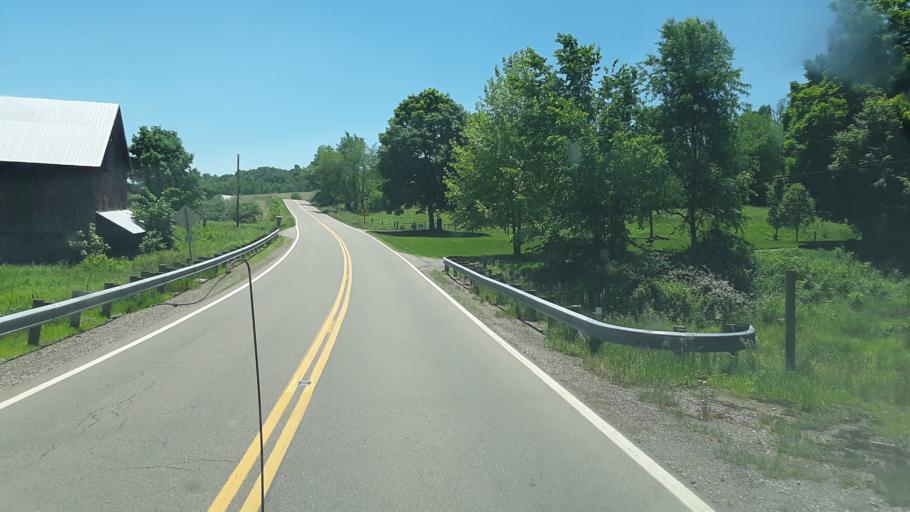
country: US
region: Ohio
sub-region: Coshocton County
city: Coshocton
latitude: 40.3152
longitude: -82.0153
